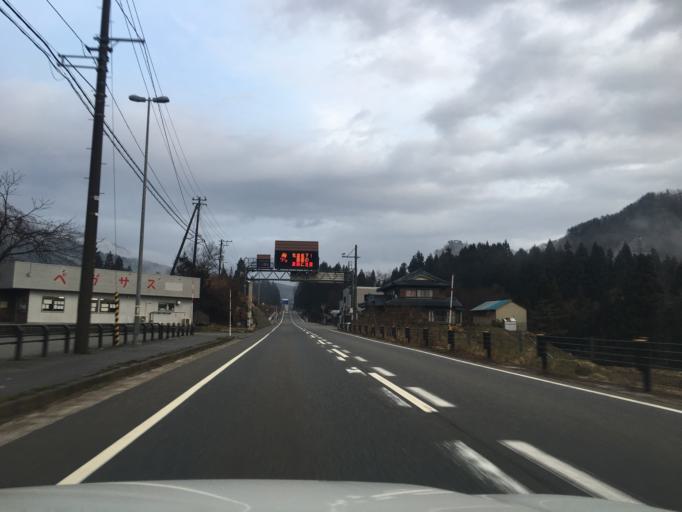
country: JP
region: Niigata
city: Murakami
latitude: 38.3609
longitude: 139.5525
